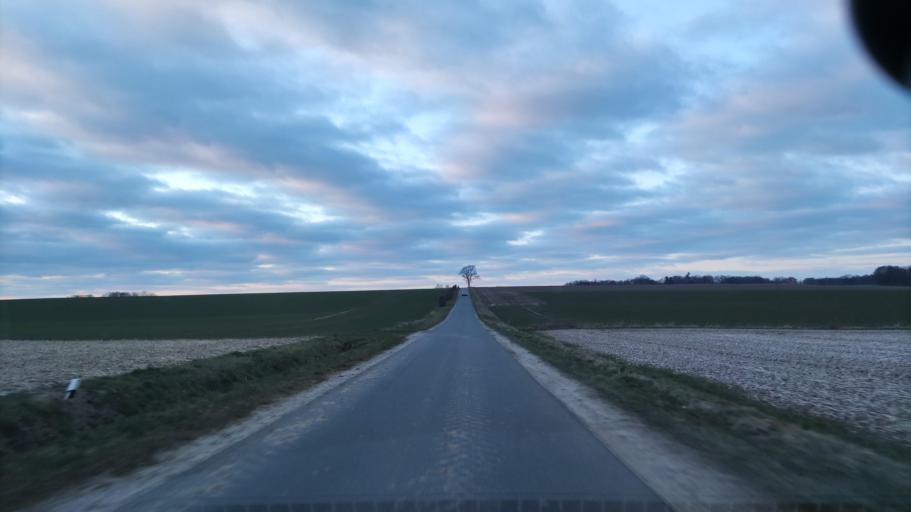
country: DE
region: Lower Saxony
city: Natendorf
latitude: 53.0599
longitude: 10.4491
